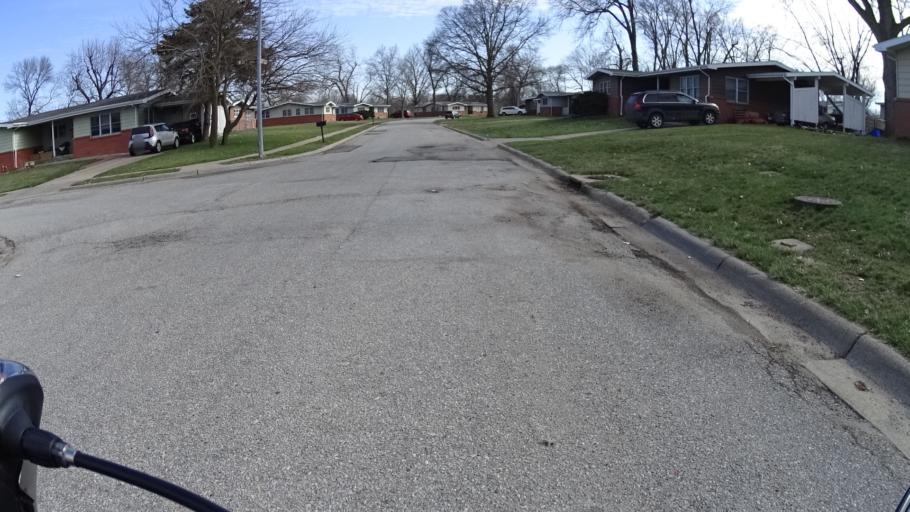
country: US
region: Nebraska
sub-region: Sarpy County
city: Offutt Air Force Base
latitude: 41.1200
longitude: -95.9586
